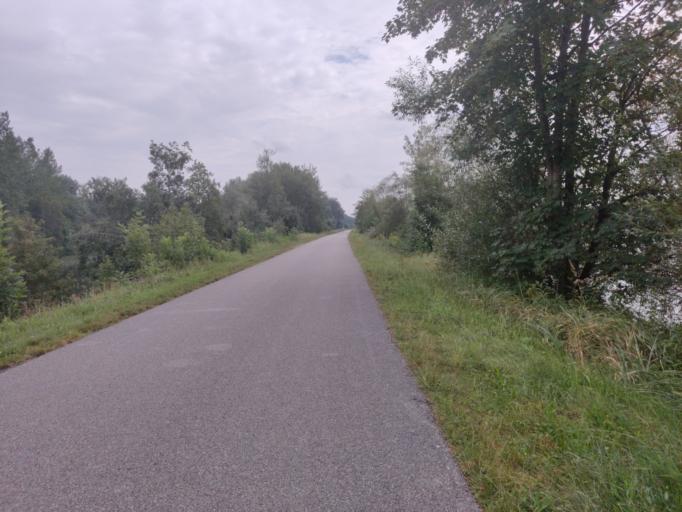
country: AT
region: Upper Austria
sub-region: Politischer Bezirk Perg
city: Perg
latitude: 48.1929
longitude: 14.6216
